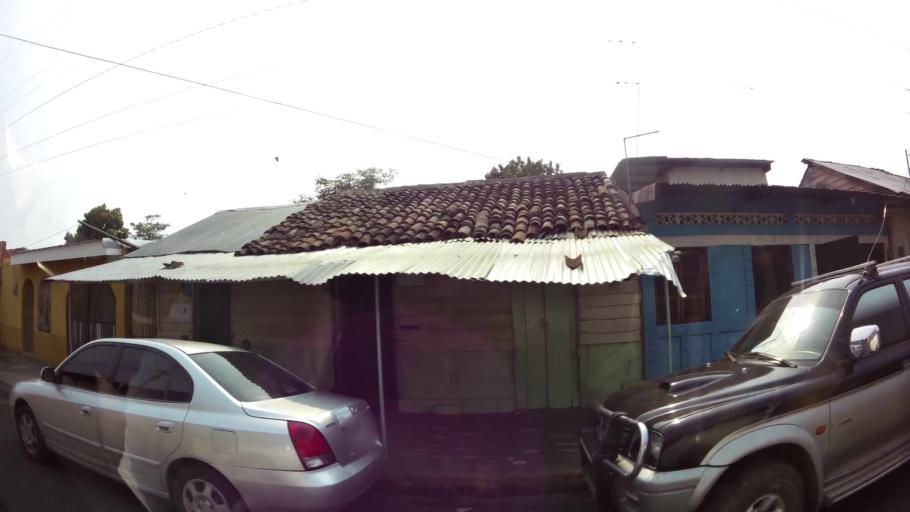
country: NI
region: Chinandega
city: Chinandega
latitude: 12.6247
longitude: -87.1336
